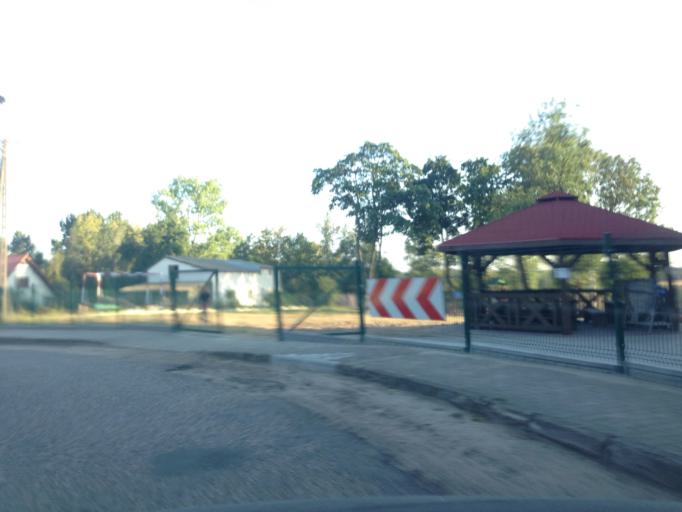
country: PL
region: Kujawsko-Pomorskie
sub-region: Powiat brodnicki
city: Brzozie
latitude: 53.2881
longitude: 19.6906
